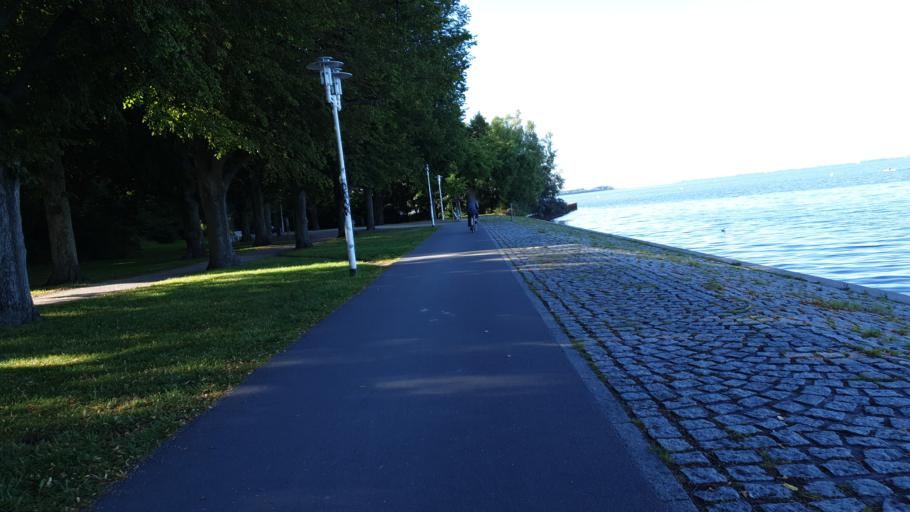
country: DE
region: Mecklenburg-Vorpommern
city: Stralsund
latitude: 54.3254
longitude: 13.0865
